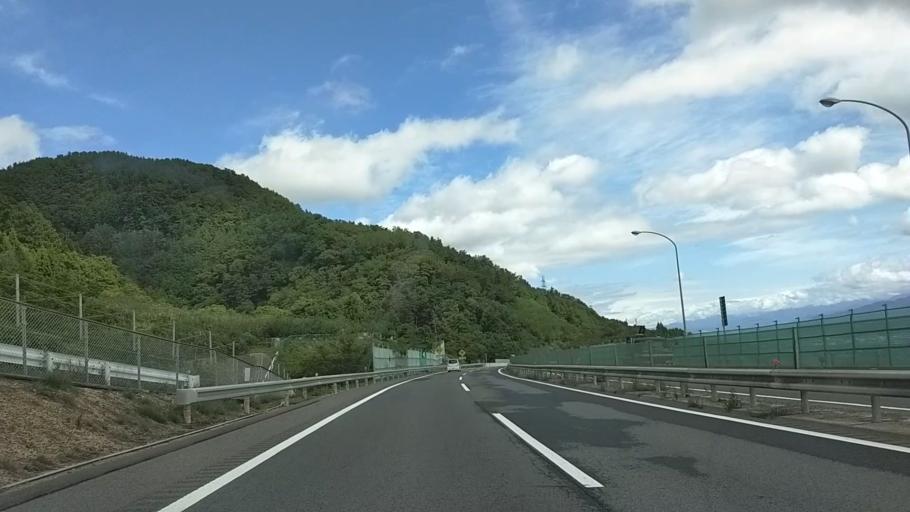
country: JP
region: Nagano
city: Nagano-shi
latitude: 36.5256
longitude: 138.0786
